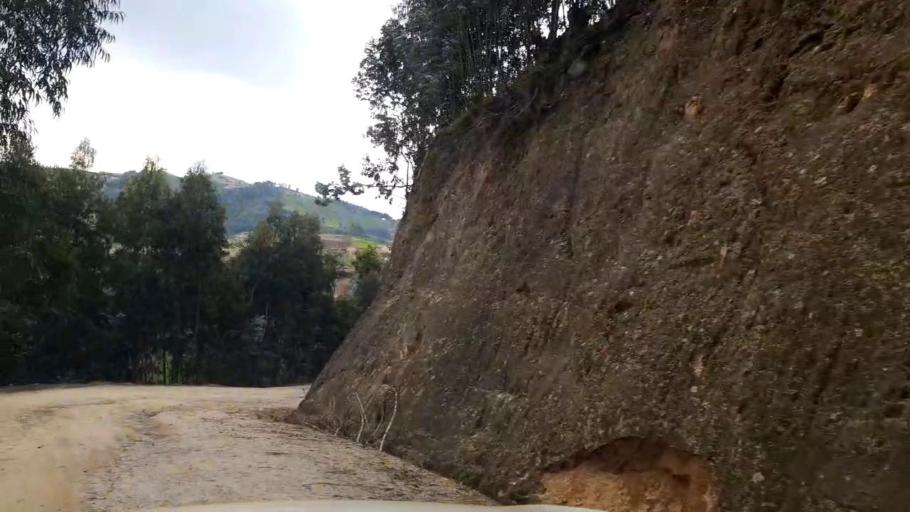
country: RW
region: Western Province
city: Kibuye
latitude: -1.8643
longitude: 29.5553
